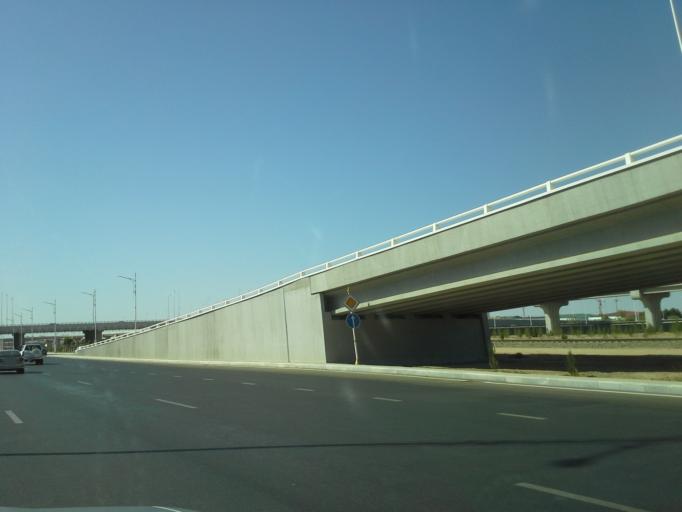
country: TM
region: Ahal
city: Ashgabat
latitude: 37.9262
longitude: 58.4309
